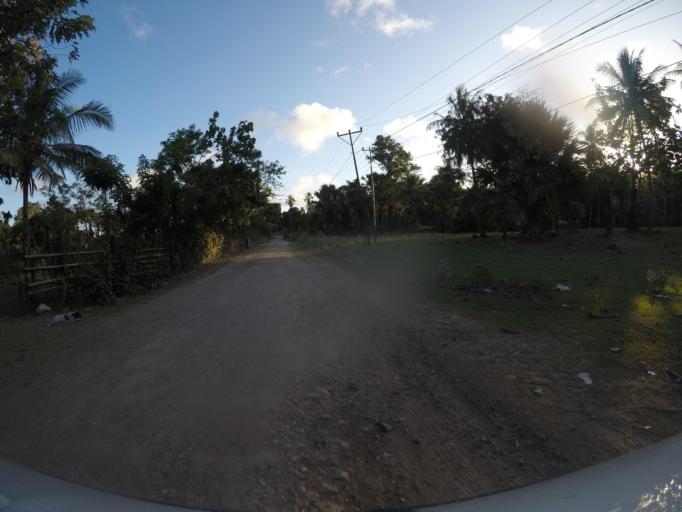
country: TL
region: Baucau
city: Venilale
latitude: -8.7406
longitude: 126.7141
